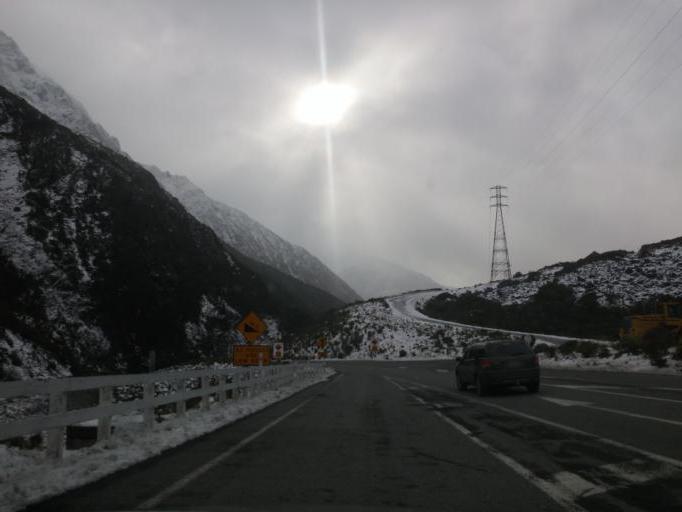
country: NZ
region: West Coast
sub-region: Grey District
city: Greymouth
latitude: -42.8905
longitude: 171.5568
